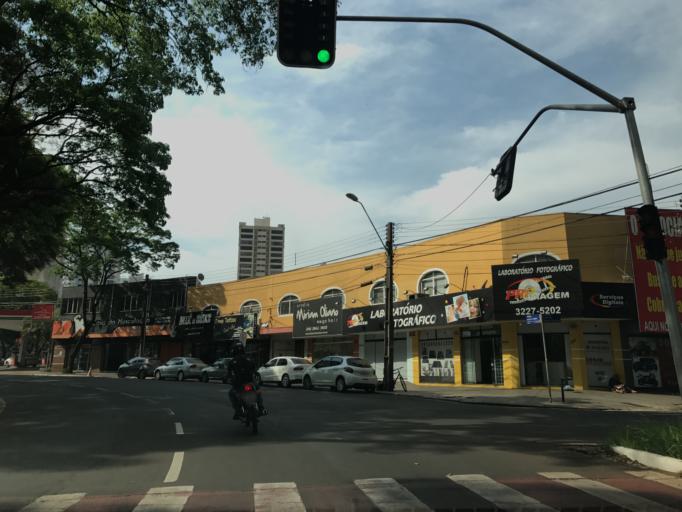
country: BR
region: Parana
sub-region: Maringa
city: Maringa
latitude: -23.4216
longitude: -51.9281
